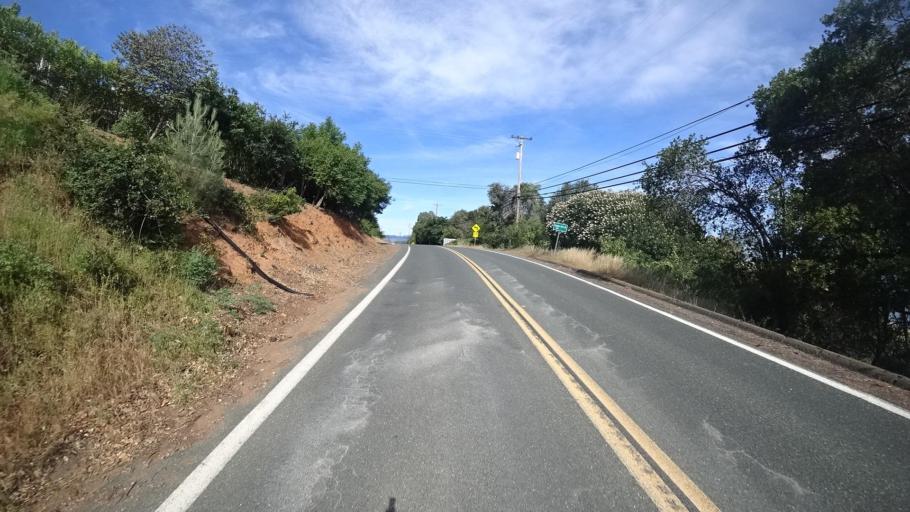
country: US
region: California
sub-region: Lake County
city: Soda Bay
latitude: 39.0092
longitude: -122.7756
